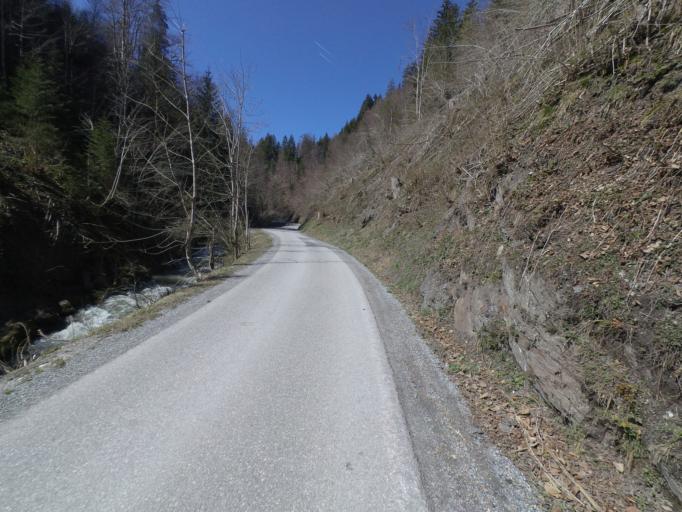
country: AT
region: Salzburg
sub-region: Politischer Bezirk Sankt Johann im Pongau
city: Sankt Veit im Pongau
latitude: 47.3274
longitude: 13.1404
